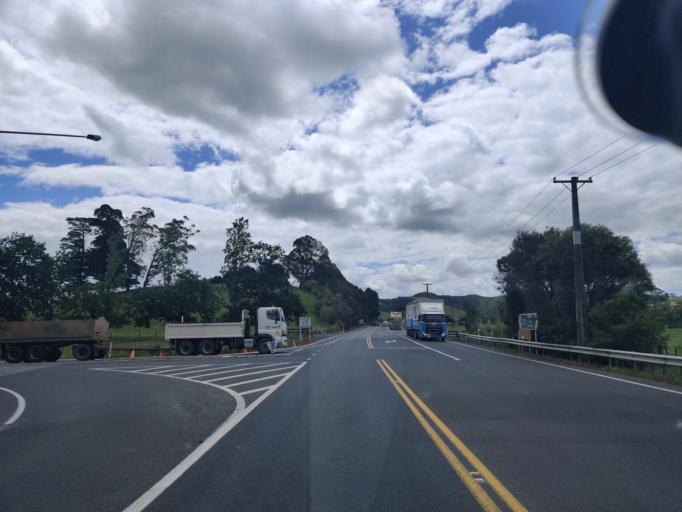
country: NZ
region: Northland
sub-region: Far North District
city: Kerikeri
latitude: -35.3017
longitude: 173.9600
